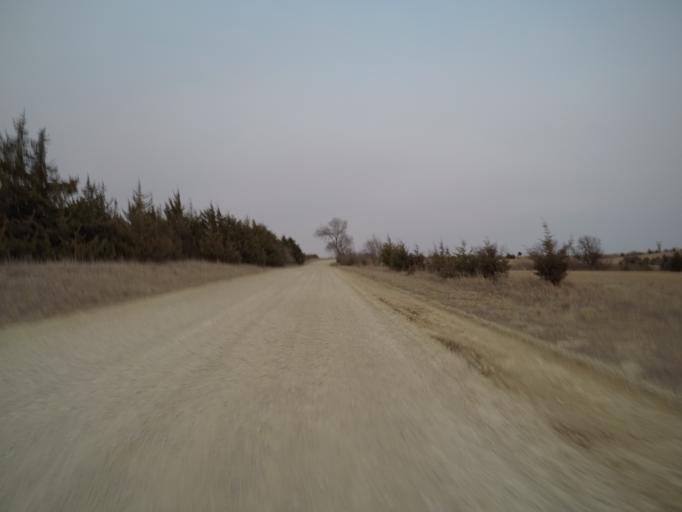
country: US
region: Kansas
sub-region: Riley County
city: Manhattan
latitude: 39.2387
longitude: -96.6528
